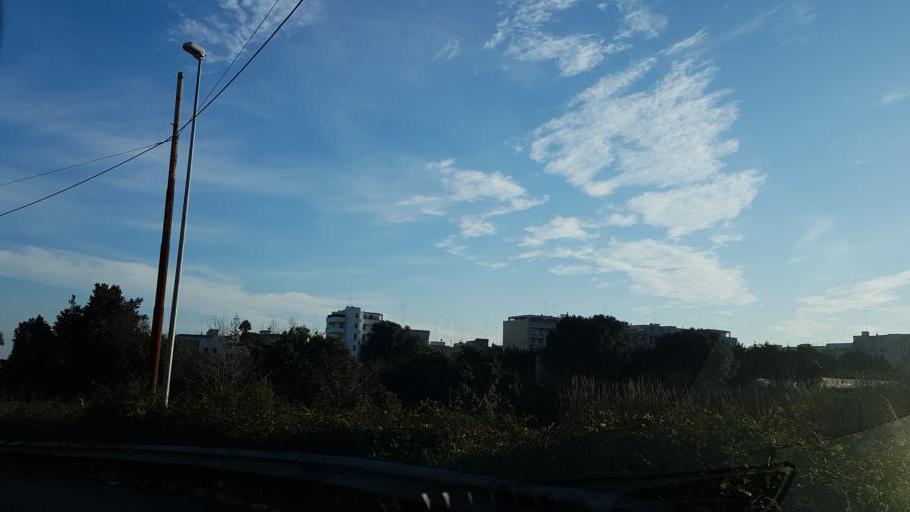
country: IT
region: Apulia
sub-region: Provincia di Brindisi
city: Brindisi
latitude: 40.6254
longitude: 17.9339
